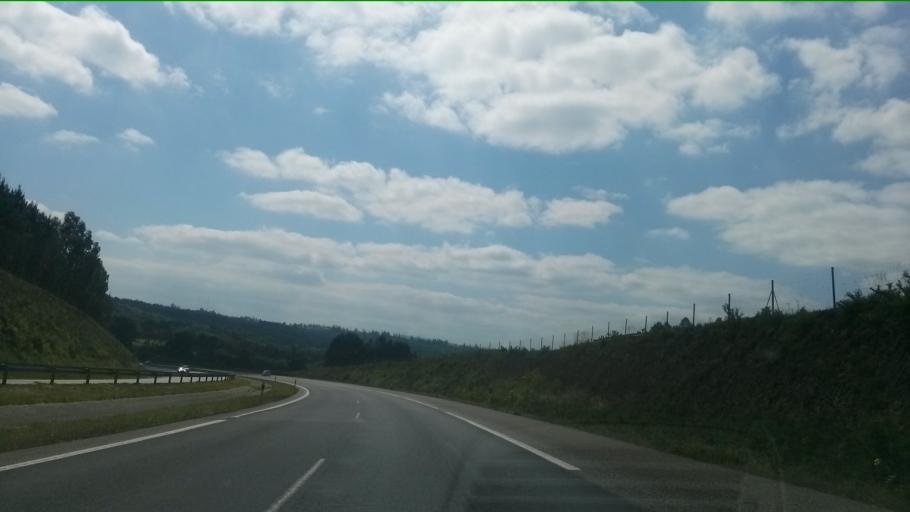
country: ES
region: Galicia
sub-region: Provincia da Coruna
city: Oroso
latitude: 42.9116
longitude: -8.4562
